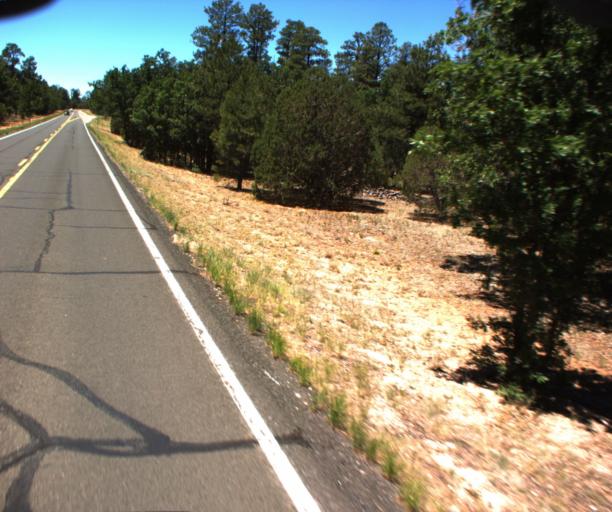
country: US
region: Arizona
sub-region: Gila County
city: Star Valley
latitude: 34.6245
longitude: -111.1524
